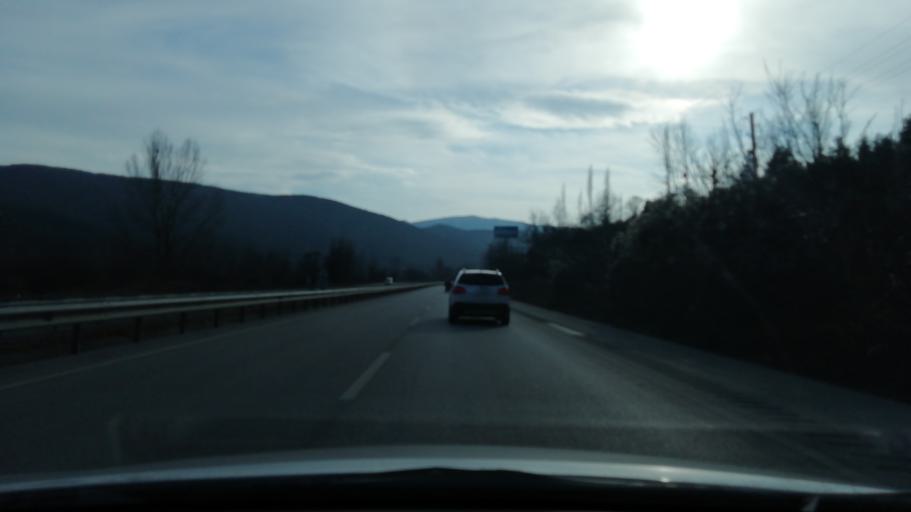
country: TR
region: Karabuk
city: Eskipazar
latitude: 41.0149
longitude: 32.6257
